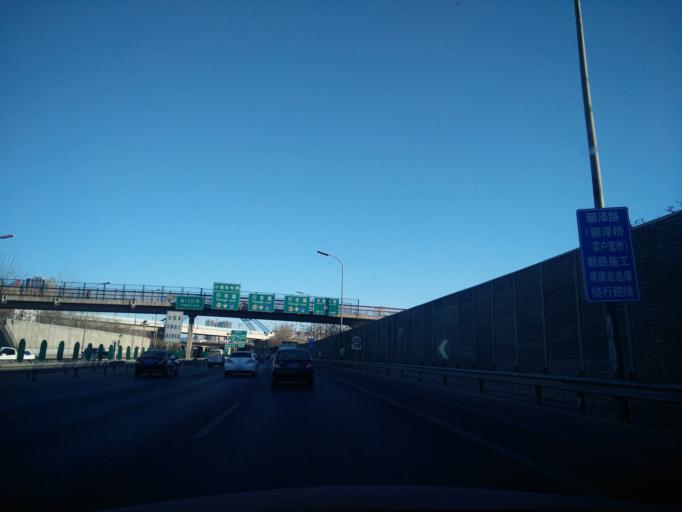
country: CN
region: Beijing
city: Lugu
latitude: 39.8876
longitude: 116.2051
